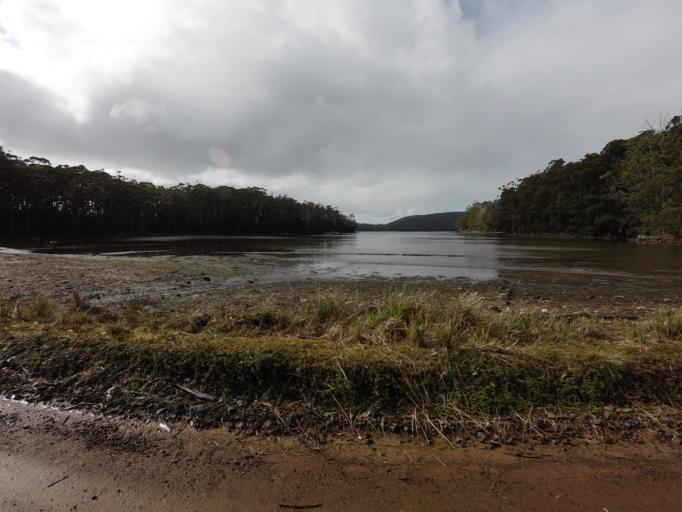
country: AU
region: Tasmania
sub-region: Huon Valley
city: Geeveston
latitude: -43.5658
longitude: 146.8870
